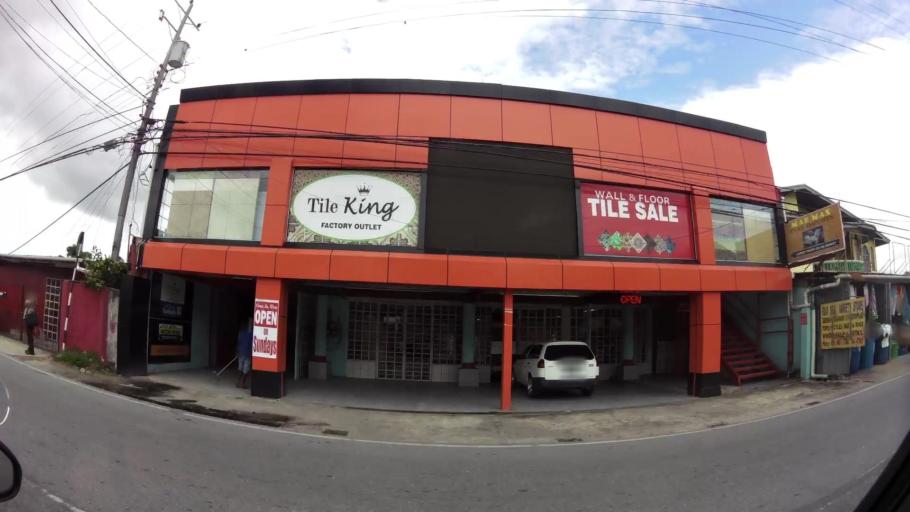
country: TT
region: Chaguanas
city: Chaguanas
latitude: 10.4825
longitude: -61.4082
